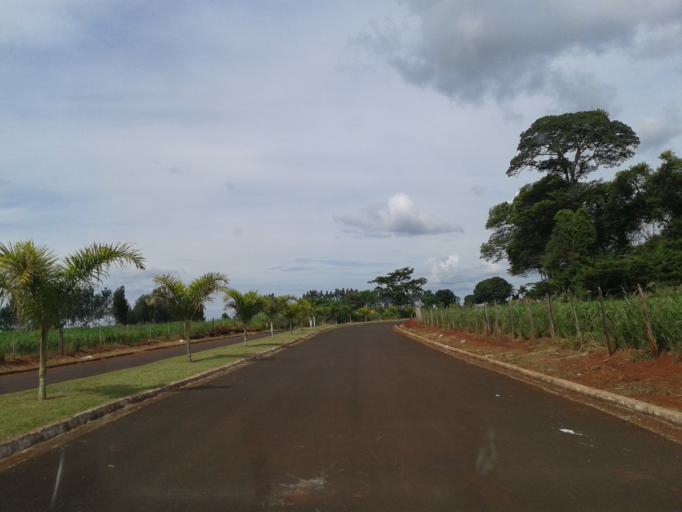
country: BR
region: Minas Gerais
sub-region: Centralina
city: Centralina
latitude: -18.5789
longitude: -49.1977
